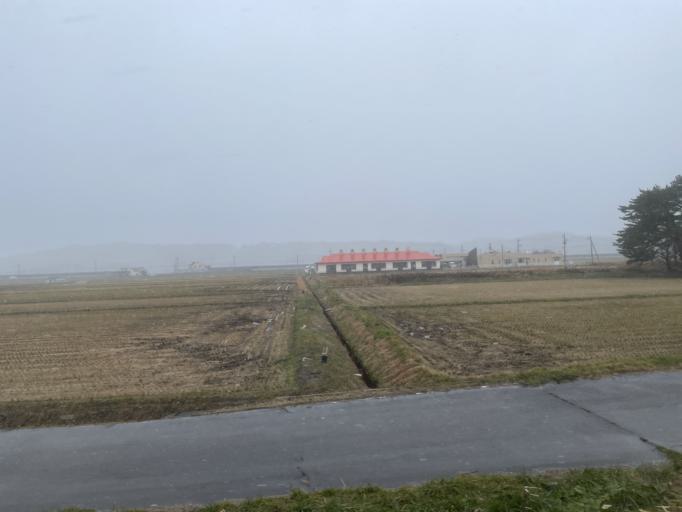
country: JP
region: Aomori
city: Aomori Shi
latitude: 40.8890
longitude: 140.6740
